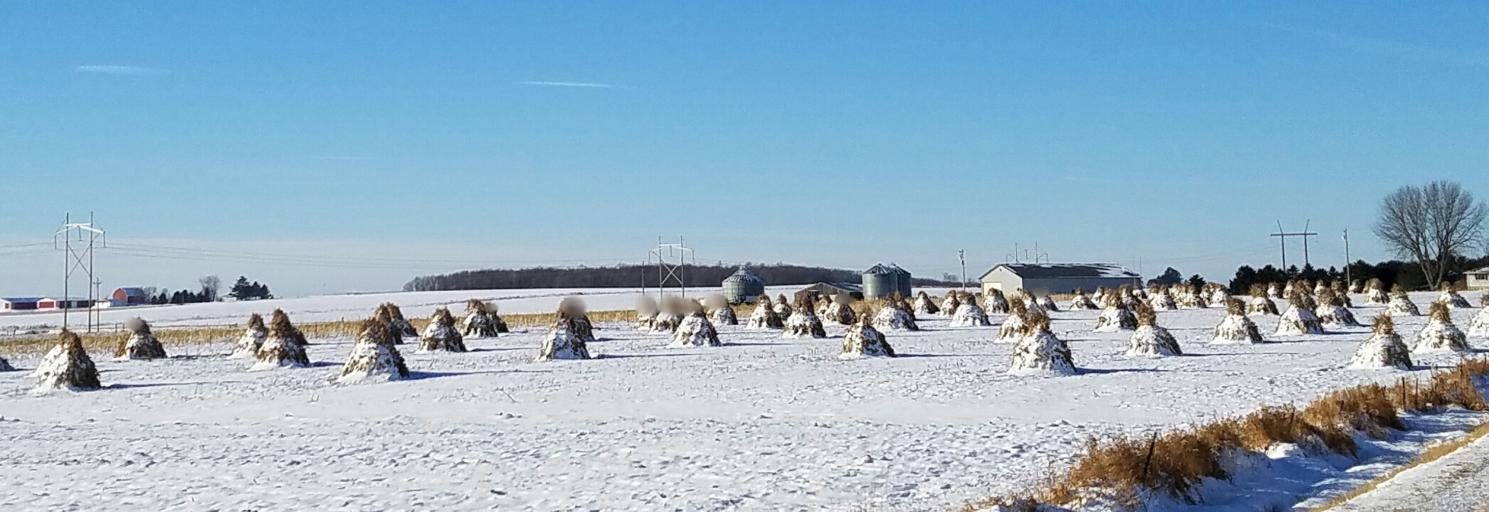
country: US
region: Wisconsin
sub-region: Clark County
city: Loyal
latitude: 44.6688
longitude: -90.4300
